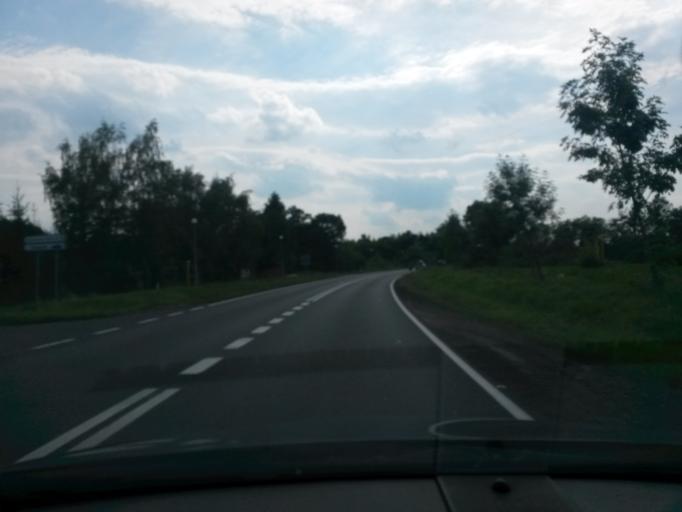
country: PL
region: Greater Poland Voivodeship
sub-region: Powiat poznanski
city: Kornik
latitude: 52.2523
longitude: 17.0743
